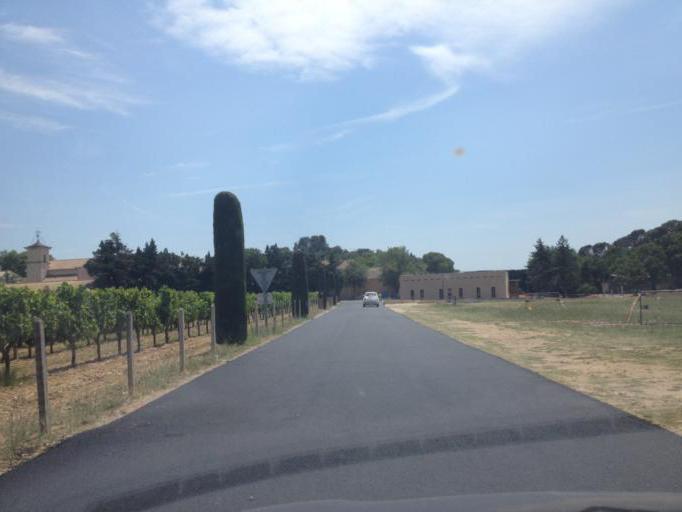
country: FR
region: Provence-Alpes-Cote d'Azur
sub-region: Departement du Vaucluse
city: Uchaux
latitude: 44.2109
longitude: 4.7998
